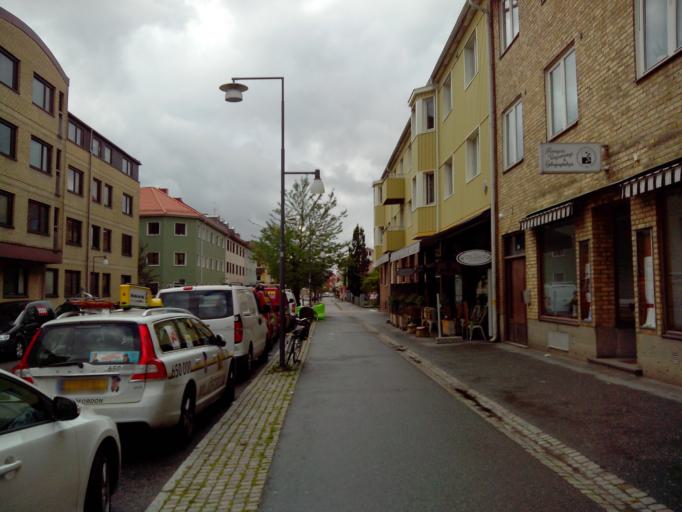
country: SE
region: Vaestra Goetaland
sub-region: Goteborg
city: Goeteborg
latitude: 57.7185
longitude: 11.9499
